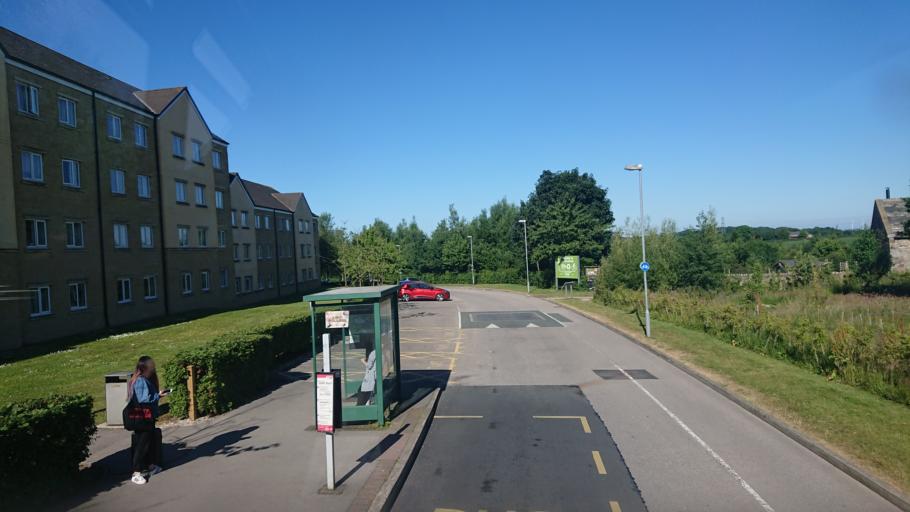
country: GB
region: England
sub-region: Lancashire
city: Galgate
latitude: 54.0055
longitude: -2.7886
